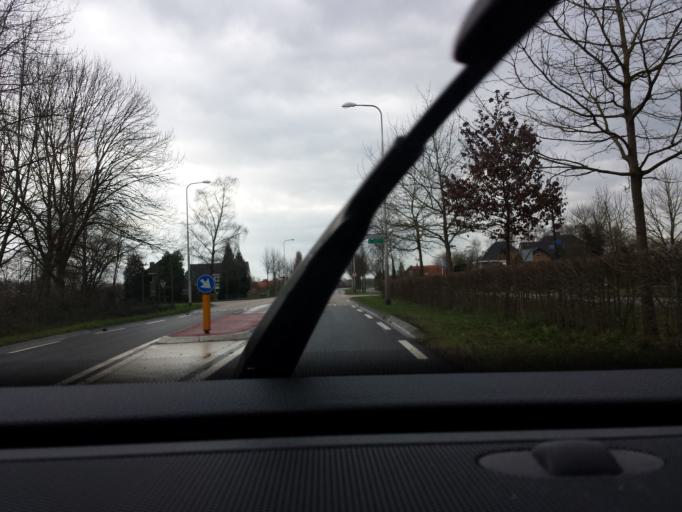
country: NL
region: Gelderland
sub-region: Oude IJsselstreek
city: Varsseveld
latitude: 51.9369
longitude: 6.4540
